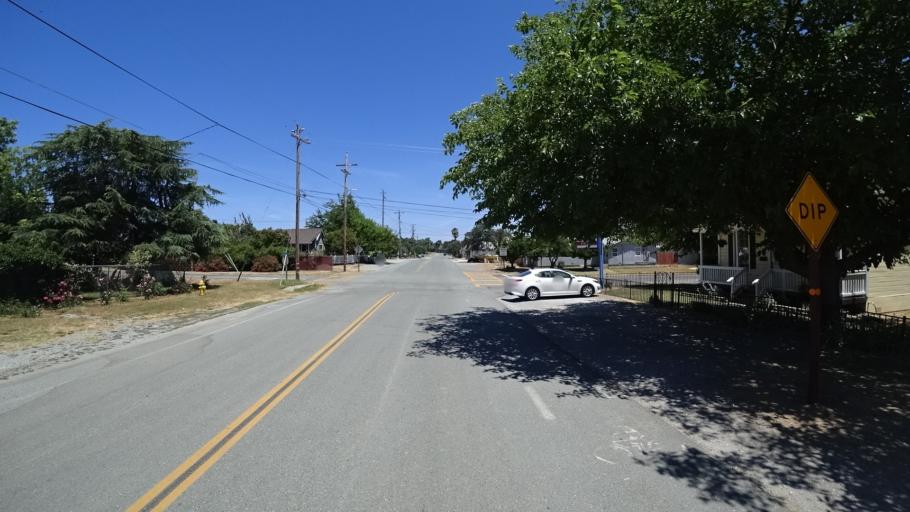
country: US
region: California
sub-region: Calaveras County
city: Valley Springs
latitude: 38.1908
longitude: -120.8309
